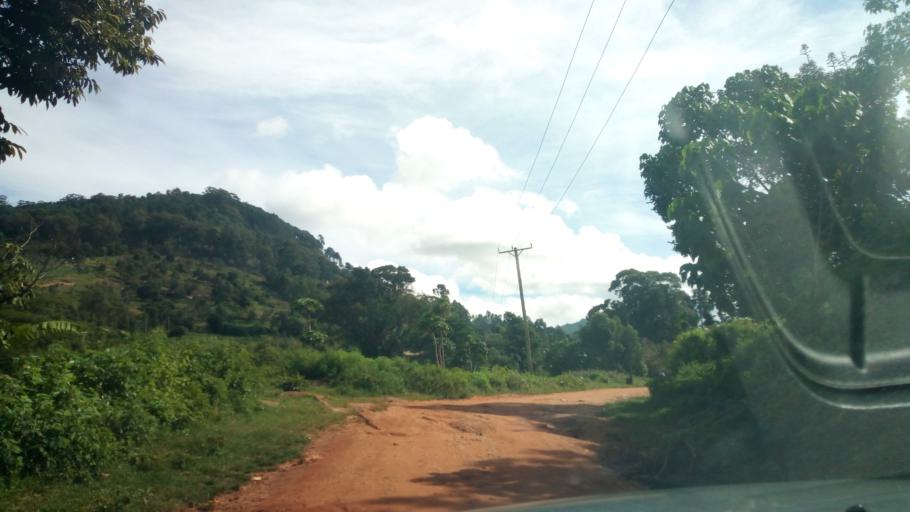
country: KE
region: Makueni
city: Wote
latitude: -1.7075
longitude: 37.4462
